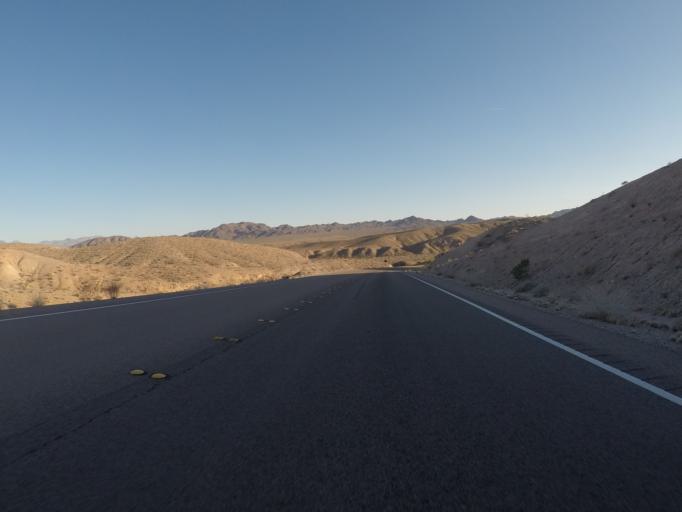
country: US
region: Nevada
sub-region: Clark County
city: Moapa Valley
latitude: 36.3121
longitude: -114.4903
